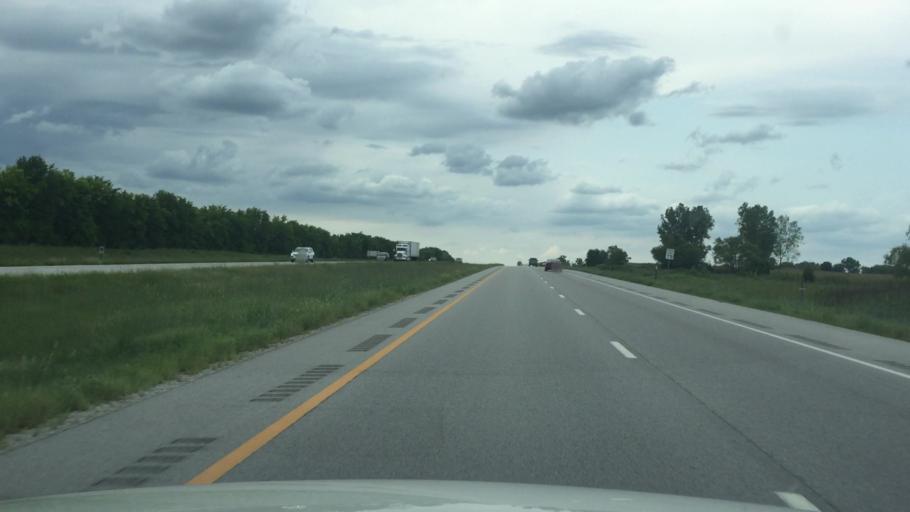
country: US
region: Kansas
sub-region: Miami County
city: Louisburg
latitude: 38.7302
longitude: -94.6763
